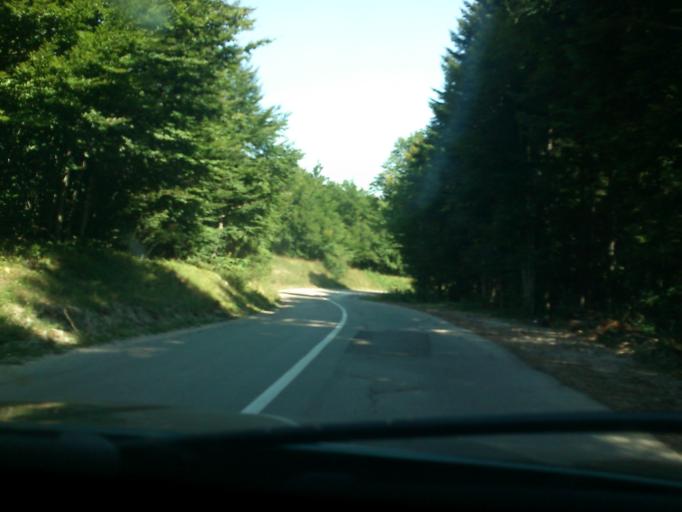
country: HR
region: Licko-Senjska
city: Brinje
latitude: 44.8449
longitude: 15.0306
